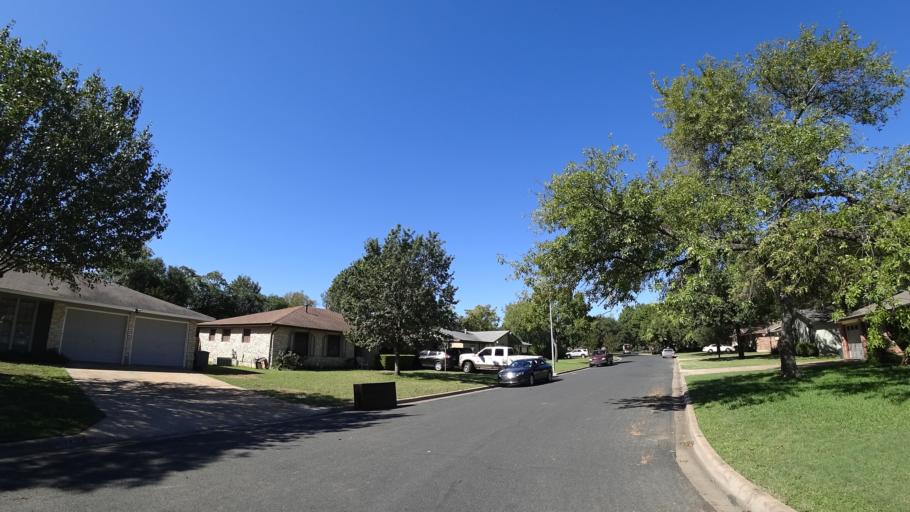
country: US
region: Texas
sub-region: Travis County
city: Rollingwood
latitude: 30.2179
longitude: -97.7981
